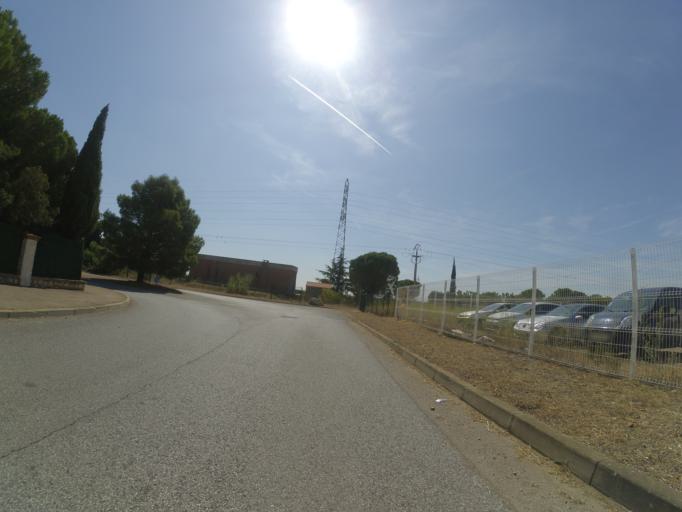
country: FR
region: Languedoc-Roussillon
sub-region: Departement des Pyrenees-Orientales
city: Salses-le-Chateau
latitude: 42.8024
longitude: 2.8945
